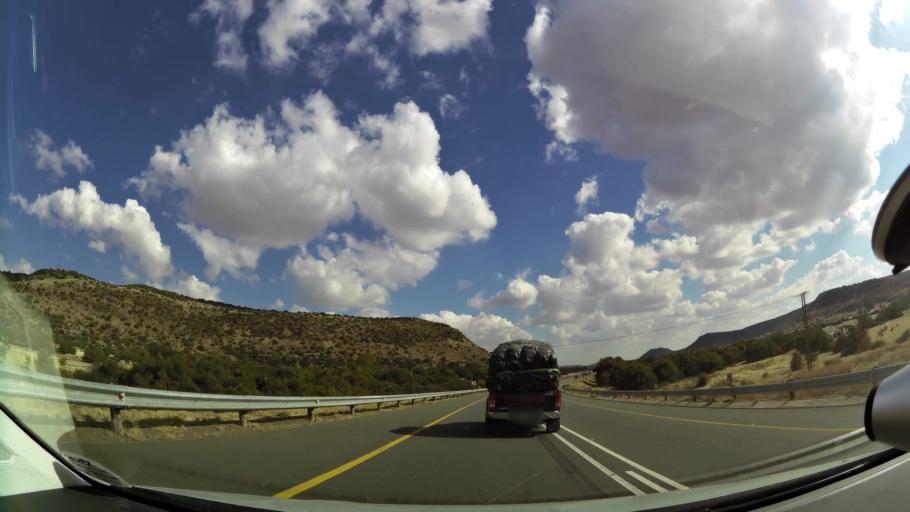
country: ZA
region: Orange Free State
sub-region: Mangaung Metropolitan Municipality
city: Bloemfontein
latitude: -29.1587
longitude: 26.0532
